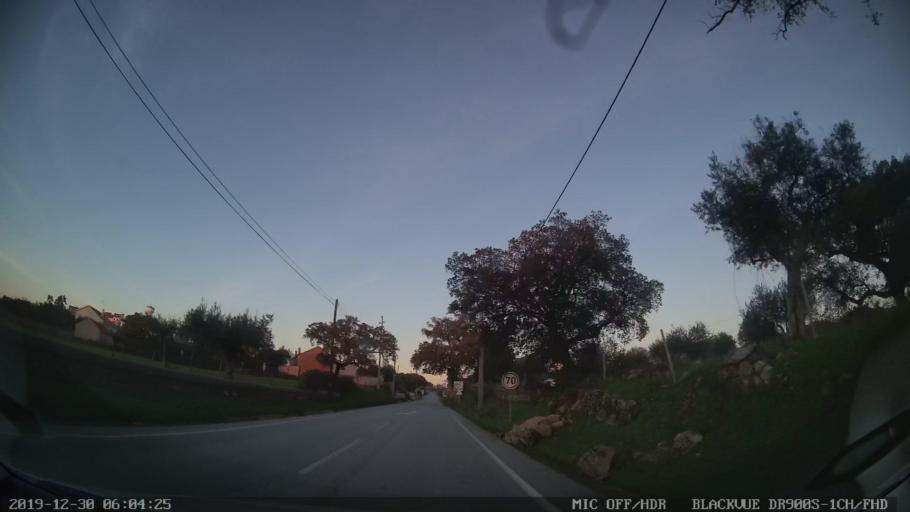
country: PT
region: Castelo Branco
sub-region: Penamacor
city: Penamacor
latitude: 40.0841
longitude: -7.2384
